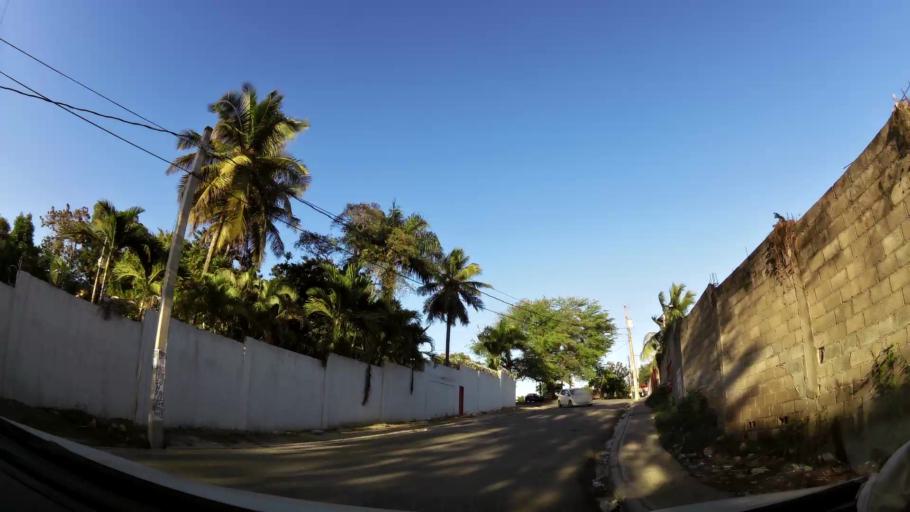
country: DO
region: Nacional
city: Santo Domingo
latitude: 18.4874
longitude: -69.9662
